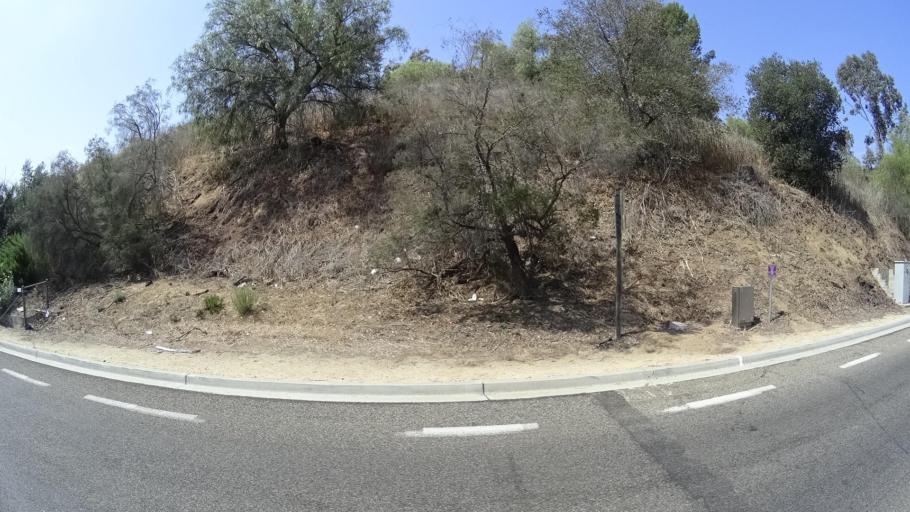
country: US
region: California
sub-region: San Diego County
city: Fallbrook
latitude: 33.3489
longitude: -117.2442
